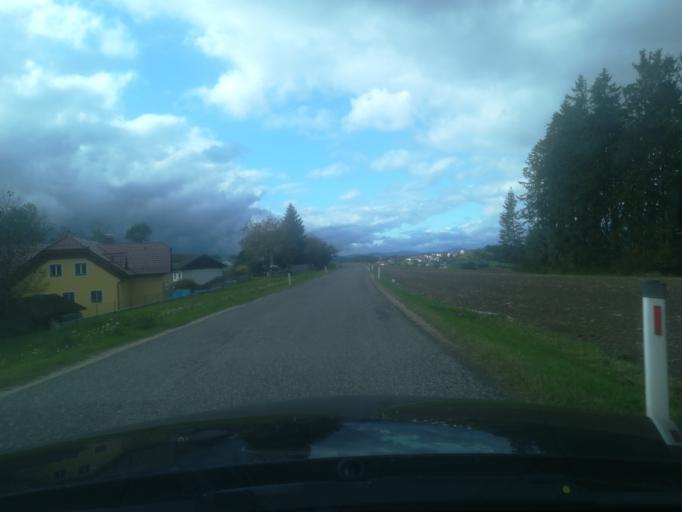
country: AT
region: Upper Austria
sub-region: Politischer Bezirk Urfahr-Umgebung
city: Herzogsdorf
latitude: 48.4230
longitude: 14.1492
